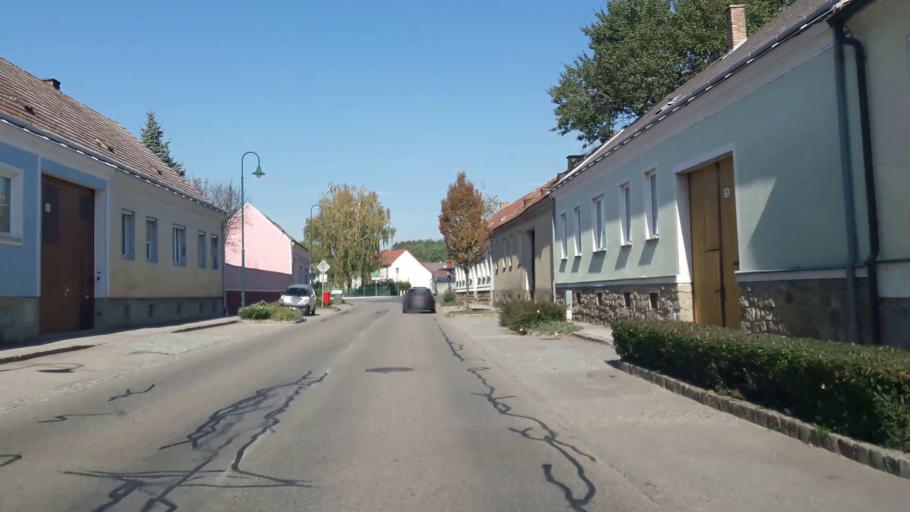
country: AT
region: Lower Austria
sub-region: Politischer Bezirk Korneuburg
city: Harmannsdorf
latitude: 48.3980
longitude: 16.3718
